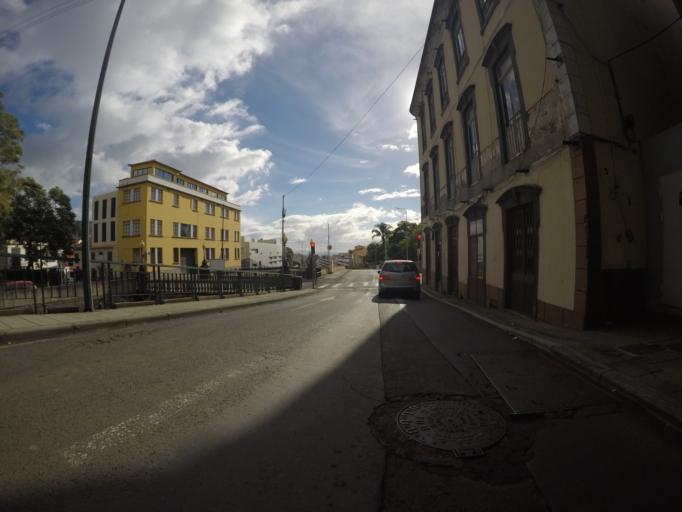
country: PT
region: Madeira
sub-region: Funchal
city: Funchal
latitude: 32.6492
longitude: -16.9184
